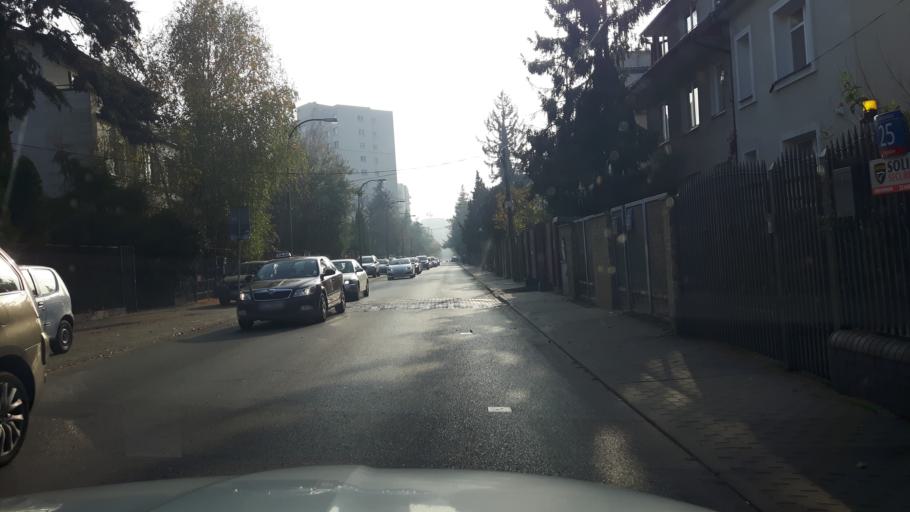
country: PL
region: Masovian Voivodeship
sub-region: Warszawa
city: Ochota
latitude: 52.1953
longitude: 20.9921
